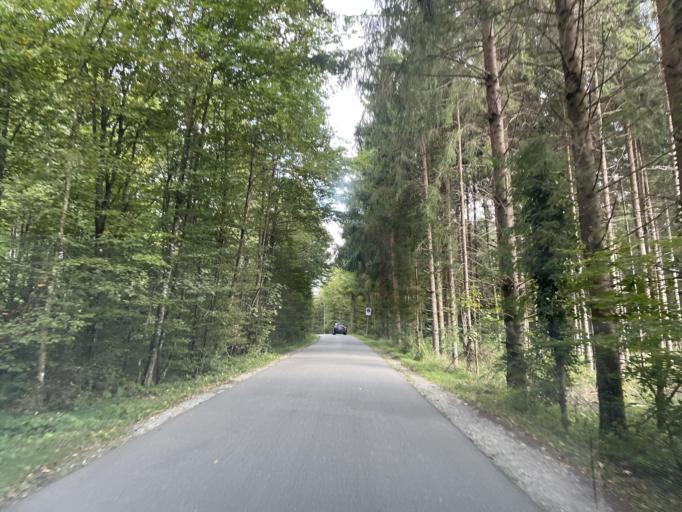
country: CH
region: Zurich
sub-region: Bezirk Winterthur
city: Mattenbach (Kreis 7)
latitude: 47.4766
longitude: 8.7335
